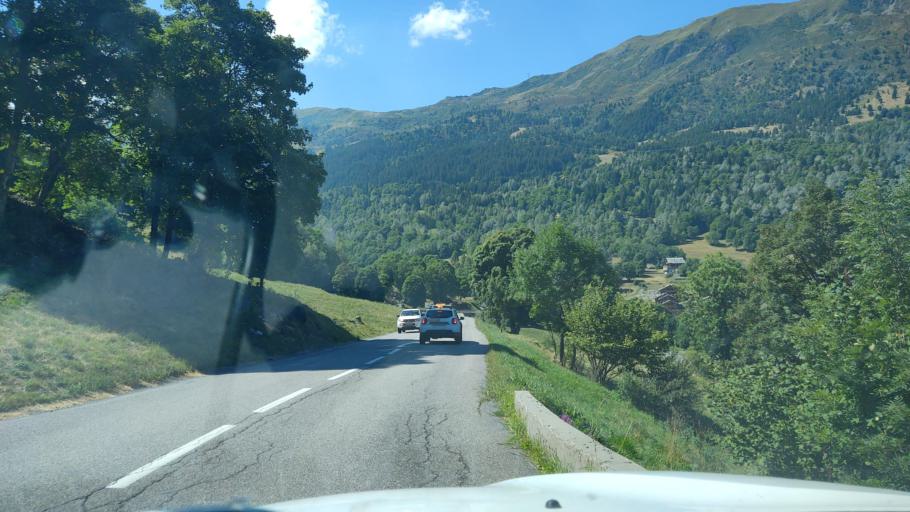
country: FR
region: Rhone-Alpes
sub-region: Departement de la Savoie
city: Meribel
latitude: 45.4113
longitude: 6.5639
